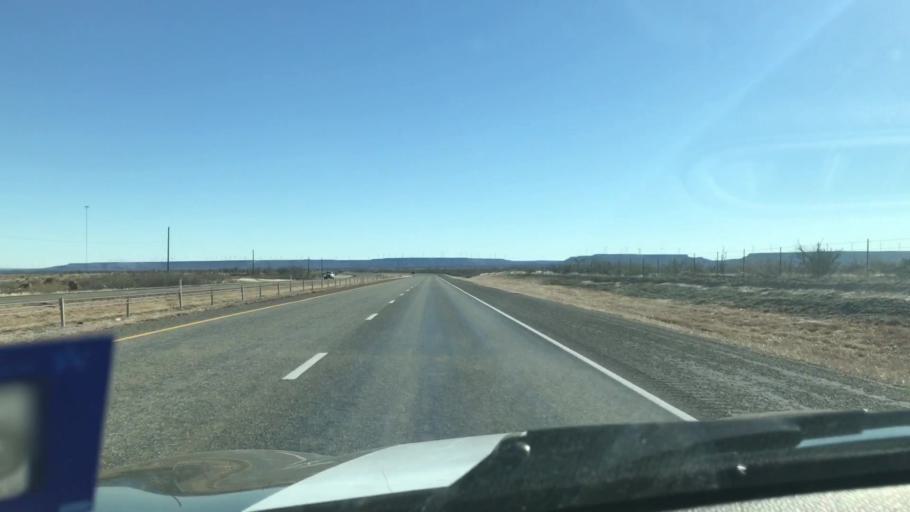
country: US
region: Texas
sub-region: Garza County
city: Post
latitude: 33.0784
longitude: -101.2388
